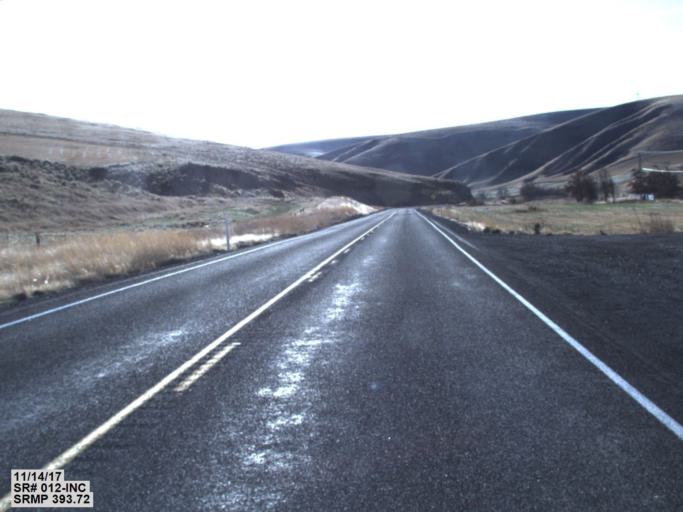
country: US
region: Washington
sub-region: Garfield County
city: Pomeroy
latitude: 46.5020
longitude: -117.7756
